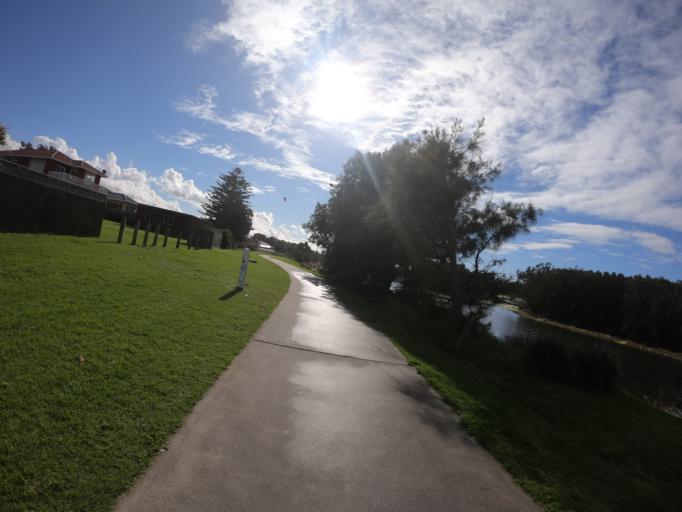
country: AU
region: New South Wales
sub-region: Wollongong
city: East Corrimal
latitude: -34.3746
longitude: 150.9193
